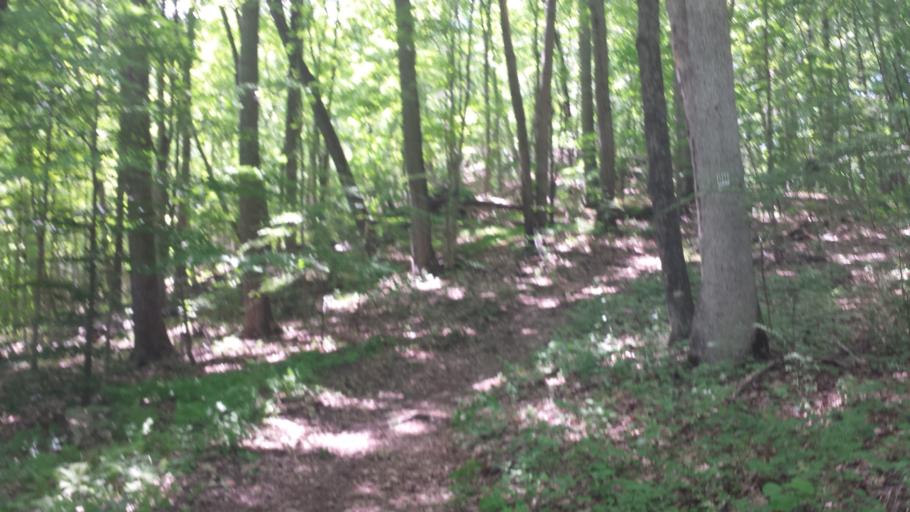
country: US
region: New York
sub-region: Westchester County
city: Pound Ridge
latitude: 41.2718
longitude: -73.5833
